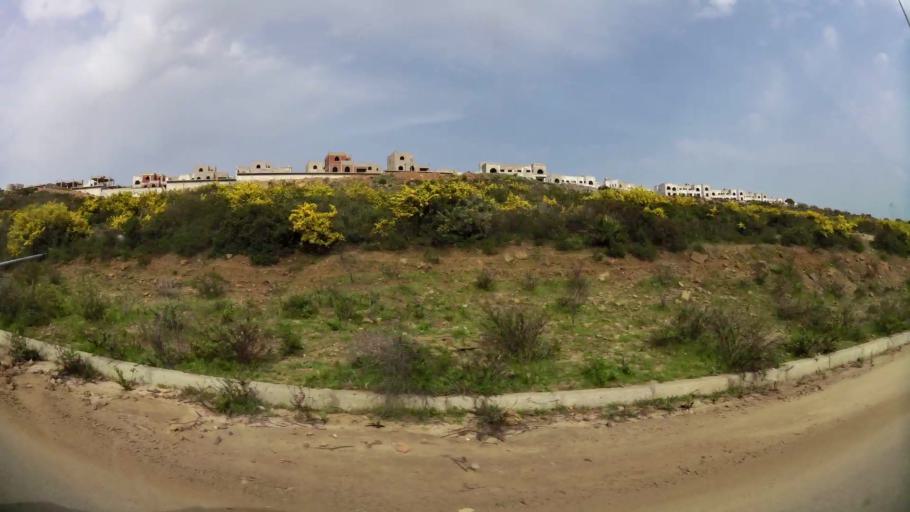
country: MA
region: Tanger-Tetouan
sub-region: Tanger-Assilah
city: Boukhalef
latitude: 35.6968
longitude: -5.9412
